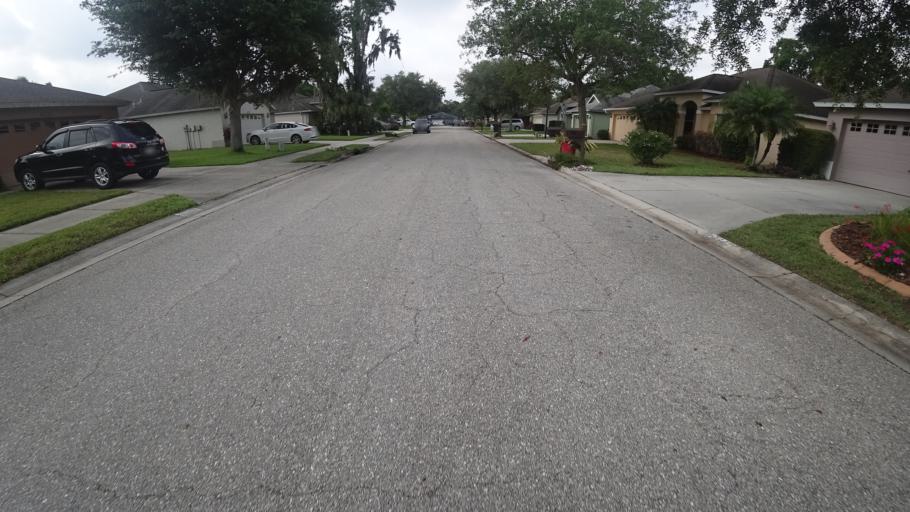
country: US
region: Florida
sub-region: Manatee County
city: Samoset
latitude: 27.4308
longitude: -82.5173
